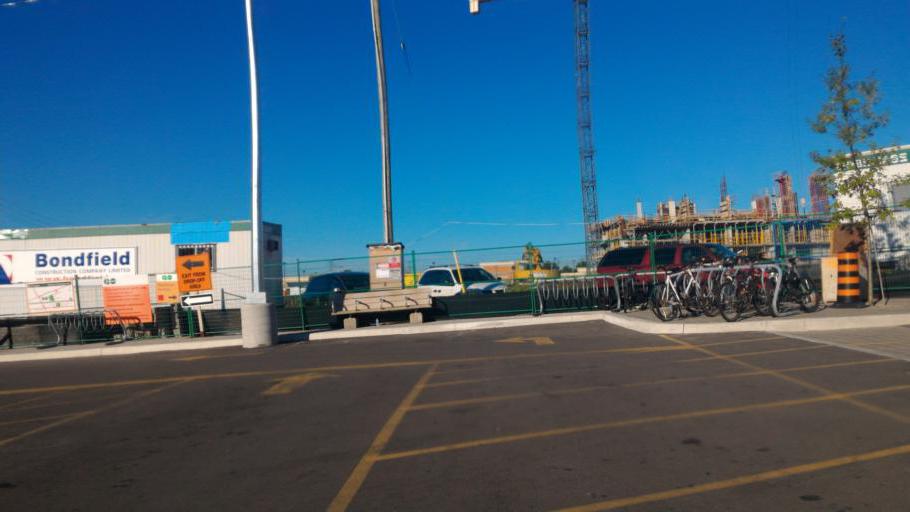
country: CA
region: Ontario
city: Burlington
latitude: 43.3400
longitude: -79.8092
